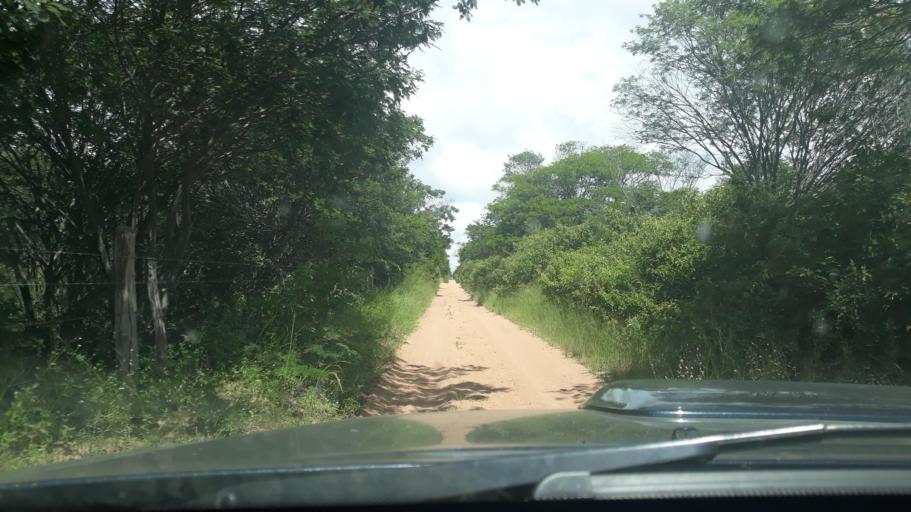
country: BR
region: Bahia
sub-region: Riacho De Santana
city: Riacho de Santana
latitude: -13.8584
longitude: -43.0397
